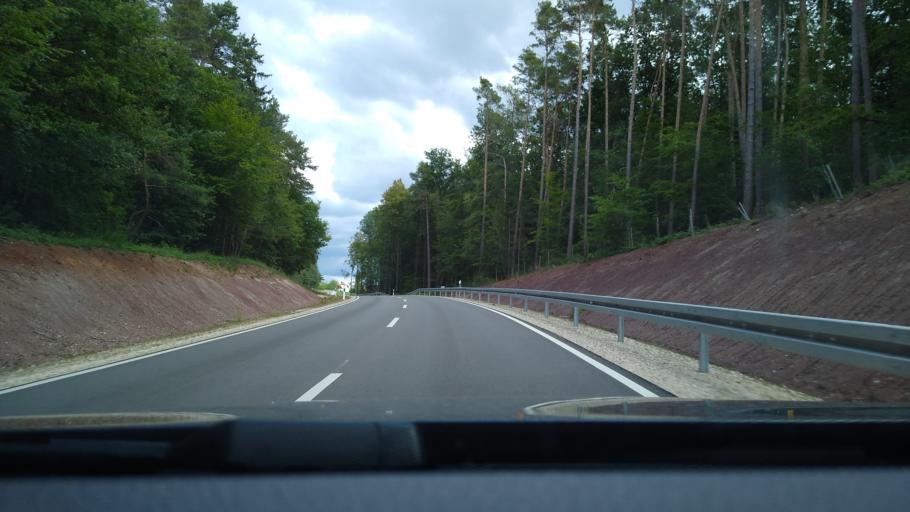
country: DE
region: Bavaria
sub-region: Regierungsbezirk Mittelfranken
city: Haundorf
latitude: 49.1495
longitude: 10.7937
